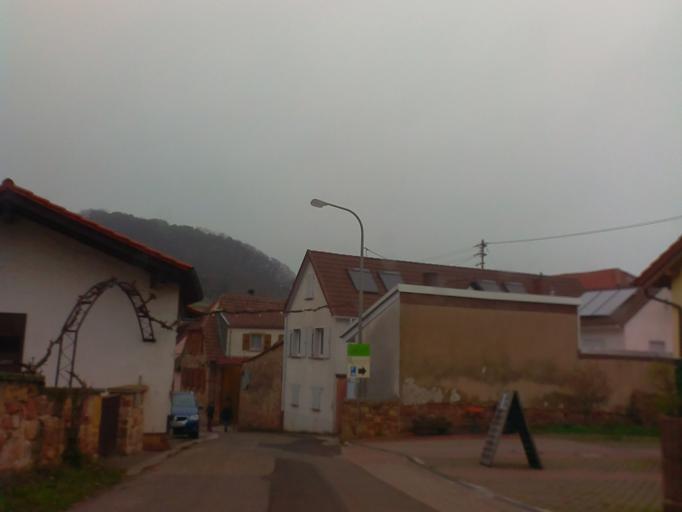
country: DE
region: Rheinland-Pfalz
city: Maikammer
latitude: 49.3211
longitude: 8.1222
